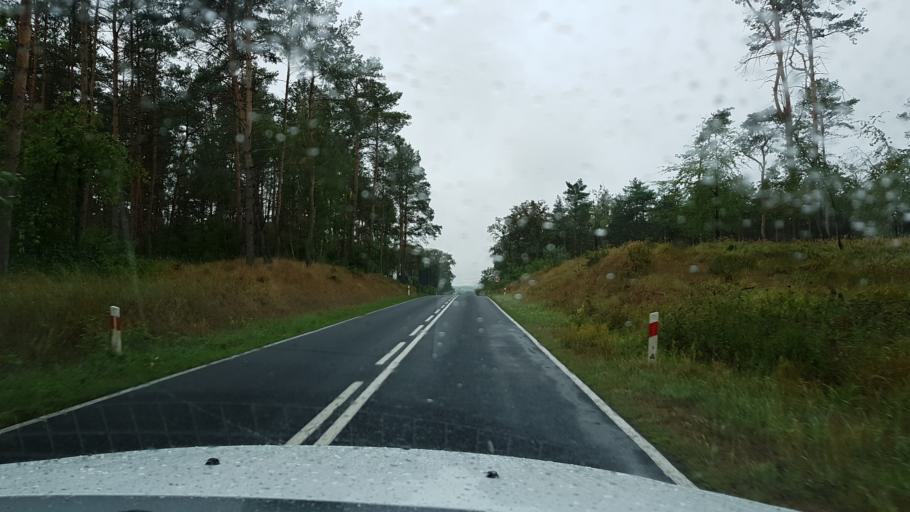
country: DE
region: Brandenburg
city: Schwedt (Oder)
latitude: 53.0392
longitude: 14.3291
